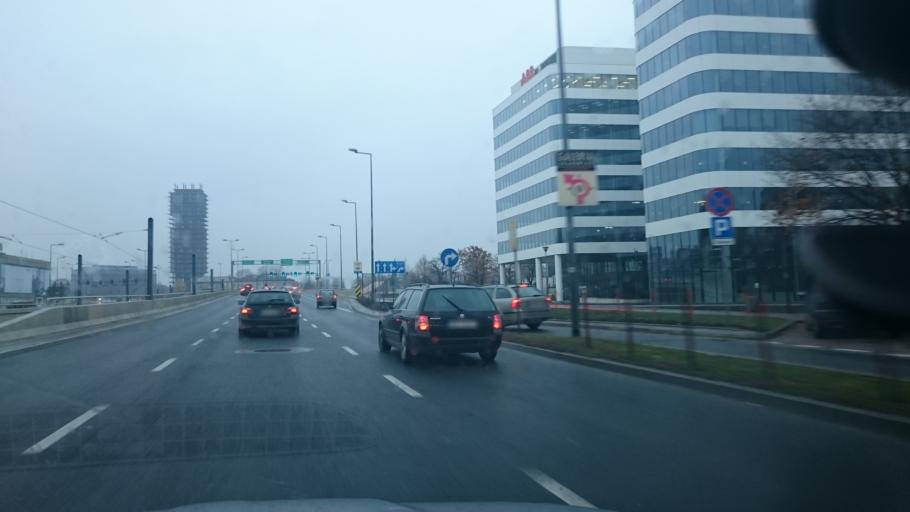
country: PL
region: Lesser Poland Voivodeship
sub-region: Krakow
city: Krakow
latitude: 50.0633
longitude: 19.9602
